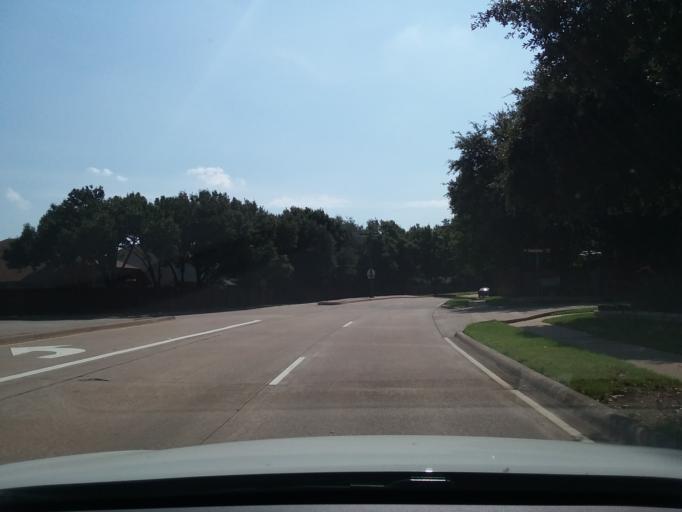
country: US
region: Texas
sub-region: Denton County
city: Flower Mound
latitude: 33.0201
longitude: -97.0597
